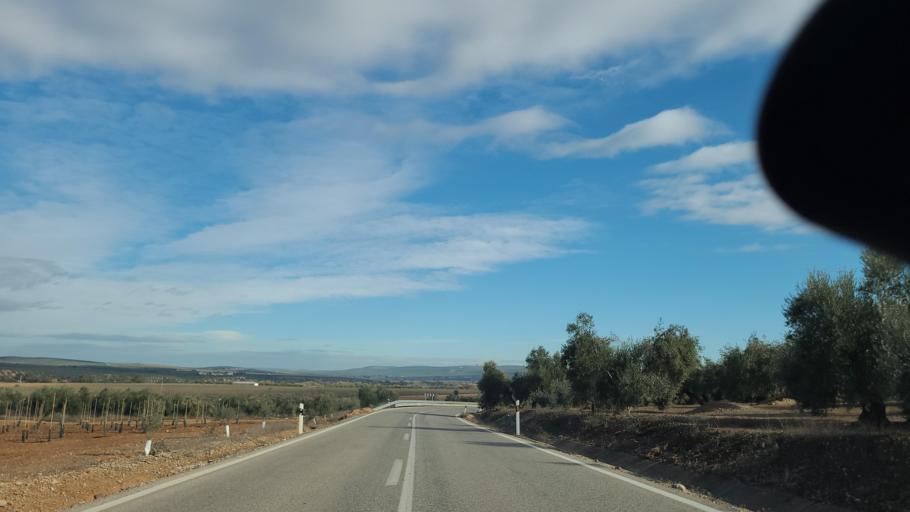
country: ES
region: Andalusia
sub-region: Provincia de Jaen
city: Espeluy
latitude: 38.0230
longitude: -3.8489
